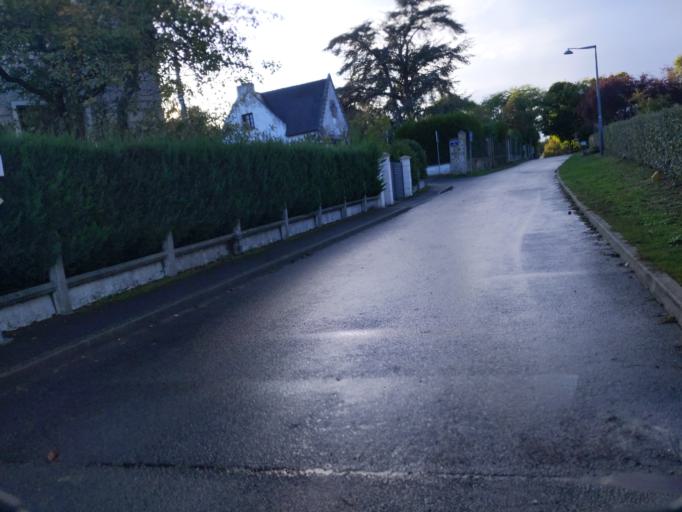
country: FR
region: Ile-de-France
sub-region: Departement des Yvelines
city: Saint-Remy-les-Chevreuse
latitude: 48.6996
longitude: 2.0987
